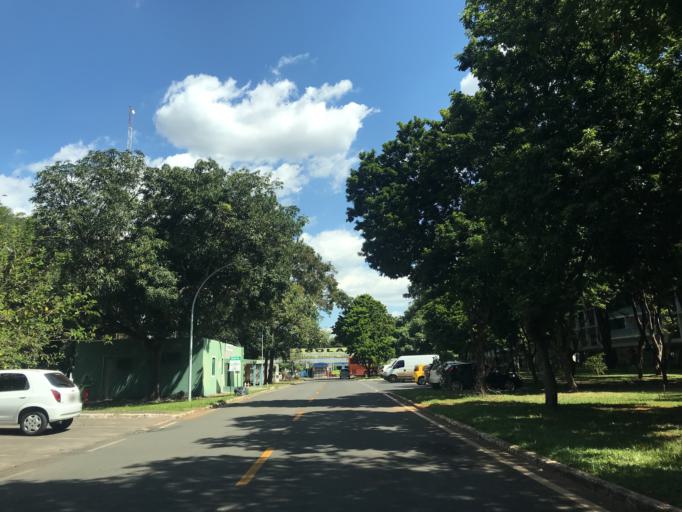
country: BR
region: Federal District
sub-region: Brasilia
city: Brasilia
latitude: -15.8361
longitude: -47.9213
